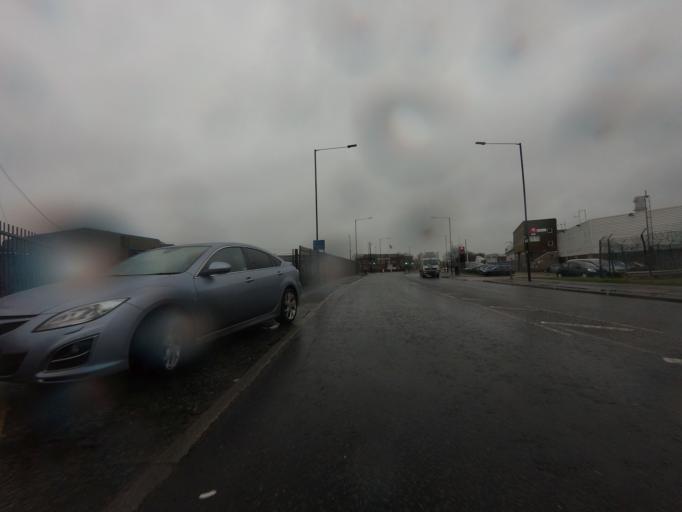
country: GB
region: England
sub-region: Hertfordshire
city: Waltham Cross
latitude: 51.6623
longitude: -0.0287
